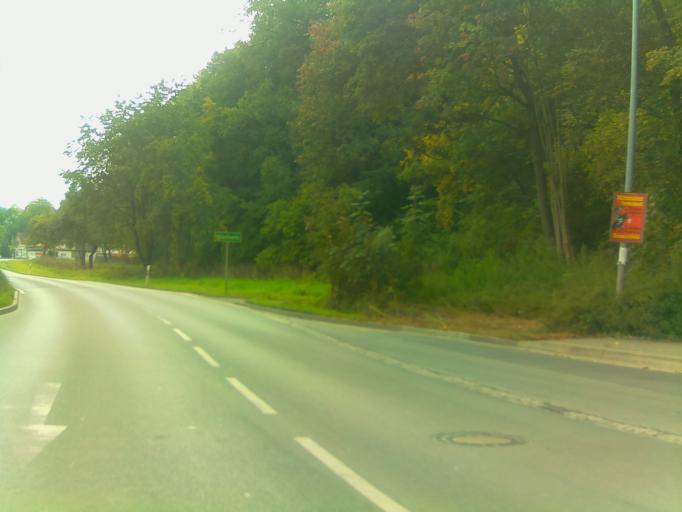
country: DE
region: Thuringia
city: Sulza
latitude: 50.8845
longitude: 11.5886
